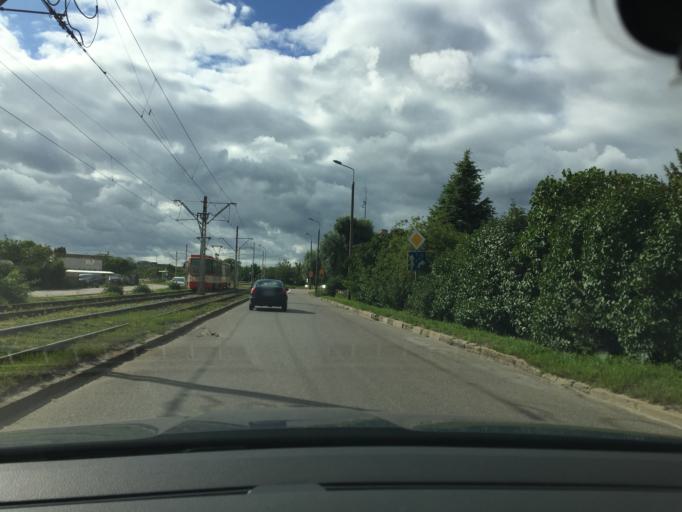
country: PL
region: Pomeranian Voivodeship
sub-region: Gdansk
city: Gdansk
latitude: 54.3620
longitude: 18.7066
